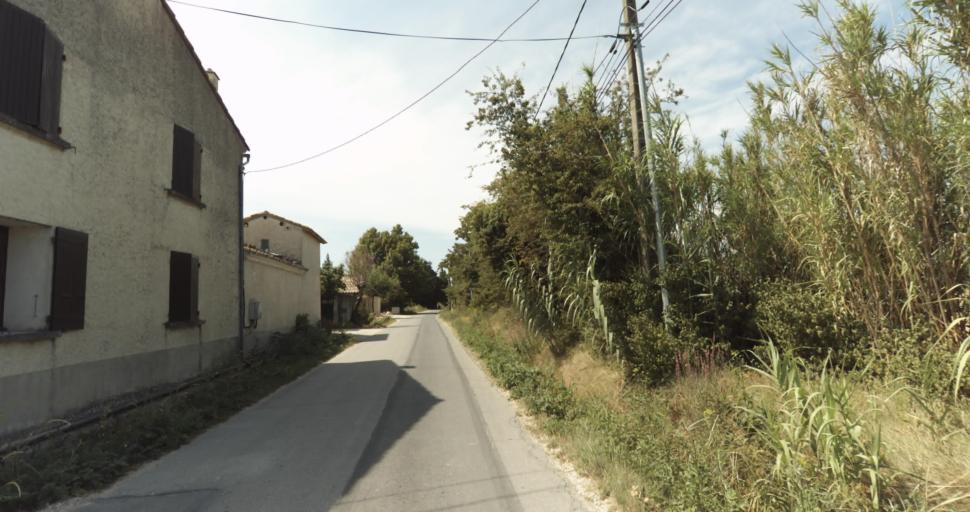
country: FR
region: Provence-Alpes-Cote d'Azur
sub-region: Departement du Vaucluse
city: Monteux
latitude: 44.0247
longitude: 4.9930
